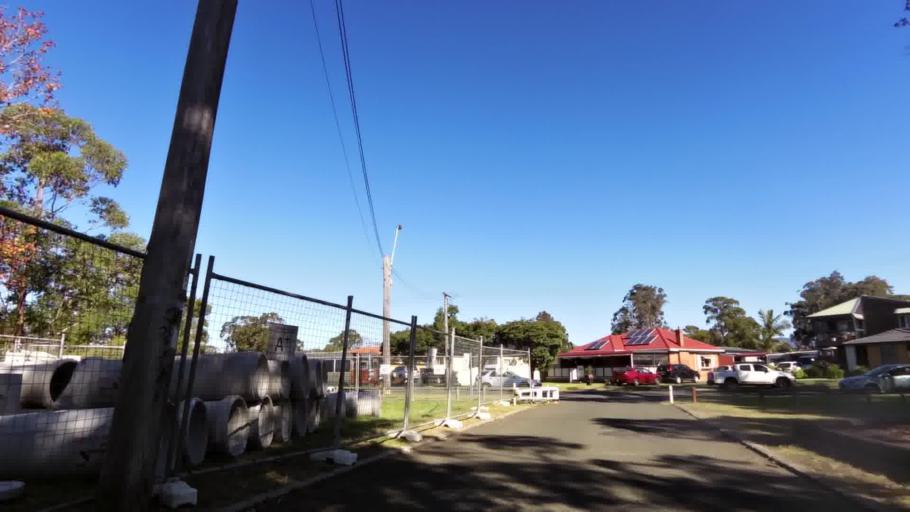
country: AU
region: New South Wales
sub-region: Shellharbour
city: Albion Park Rail
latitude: -34.5557
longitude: 150.8182
